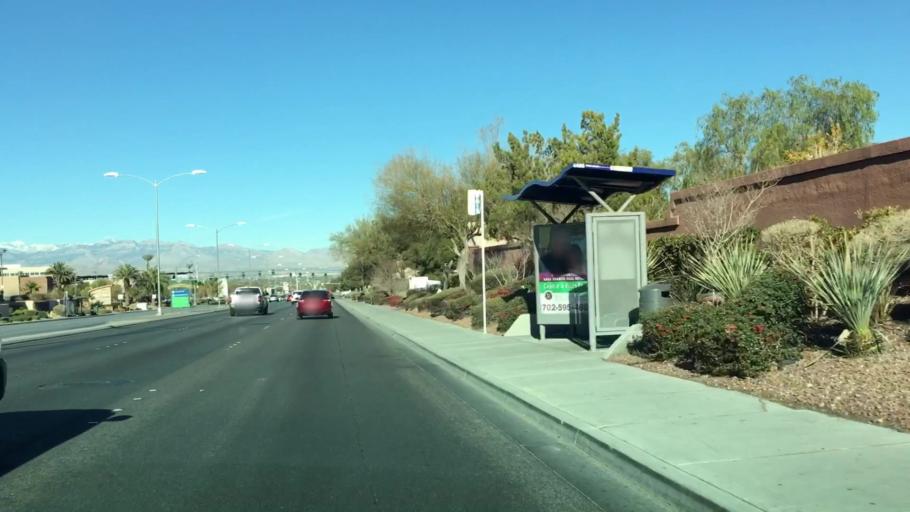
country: US
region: Nevada
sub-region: Clark County
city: Whitney
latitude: 36.0032
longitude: -115.1094
